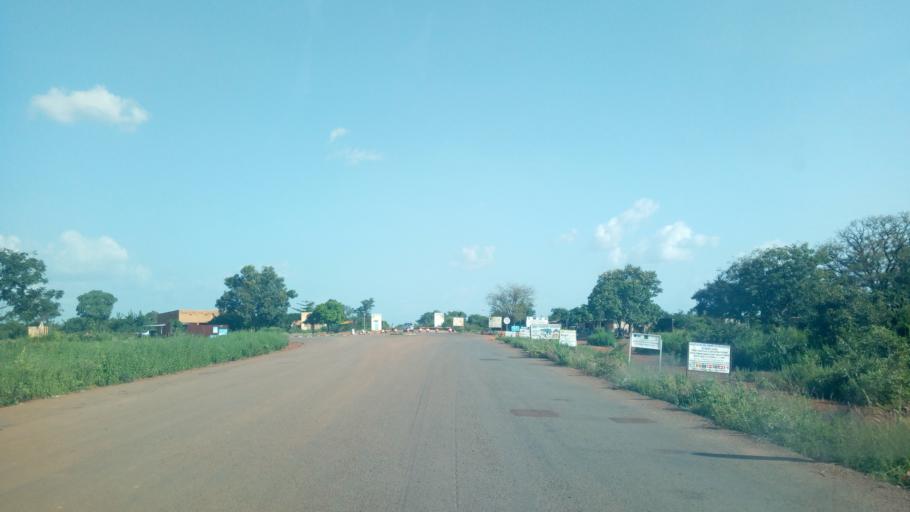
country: ML
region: Sikasso
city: Yorosso
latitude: 12.1891
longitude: -4.8429
